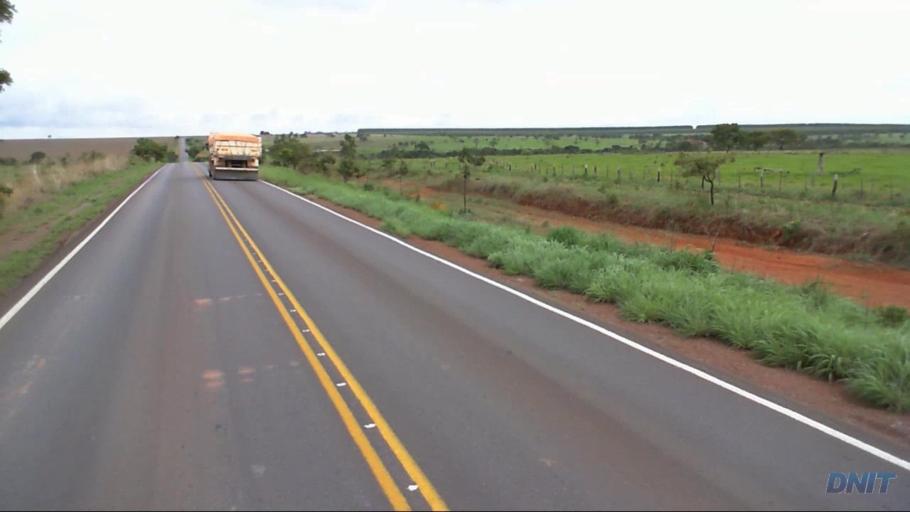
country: BR
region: Goias
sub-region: Padre Bernardo
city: Padre Bernardo
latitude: -15.2899
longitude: -48.2465
